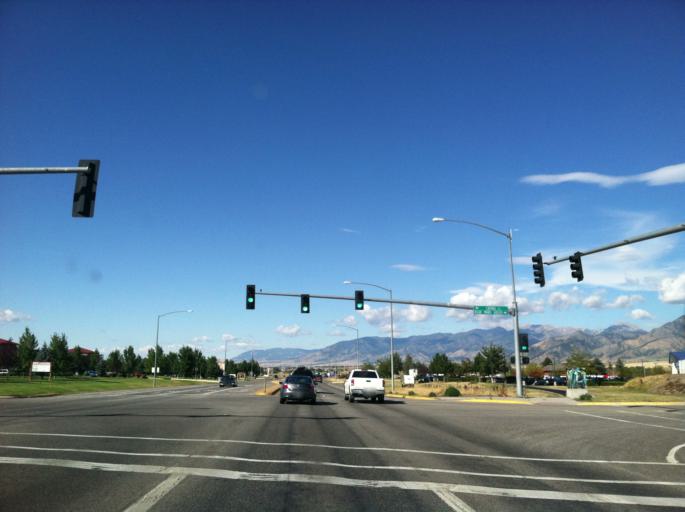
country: US
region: Montana
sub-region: Gallatin County
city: Bozeman
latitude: 45.7078
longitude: -111.0655
